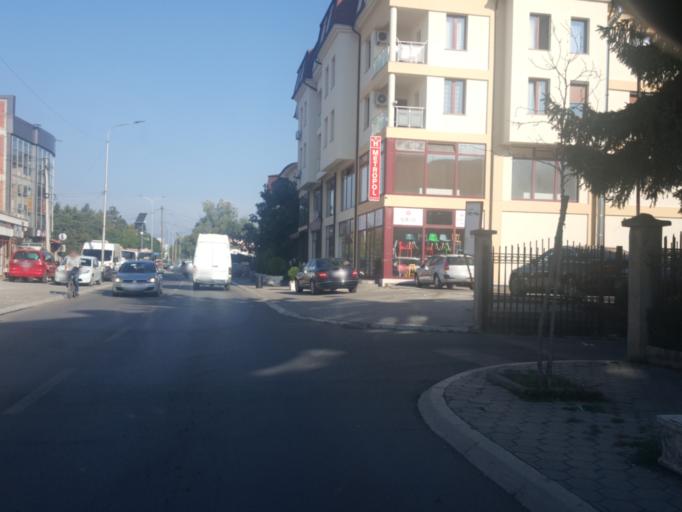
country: XK
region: Gjakova
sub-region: Komuna e Gjakoves
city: Gjakove
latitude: 42.3916
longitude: 20.4249
